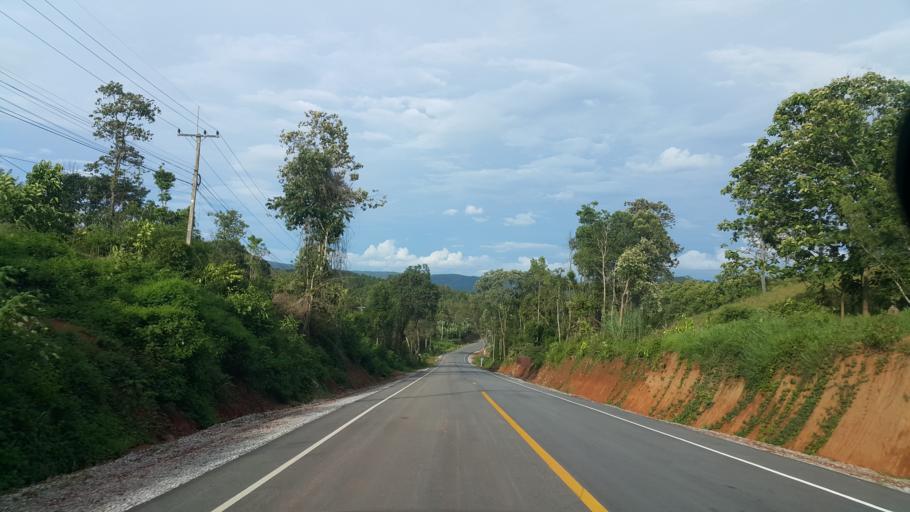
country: TH
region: Loei
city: Na Haeo
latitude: 17.4991
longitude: 101.0423
